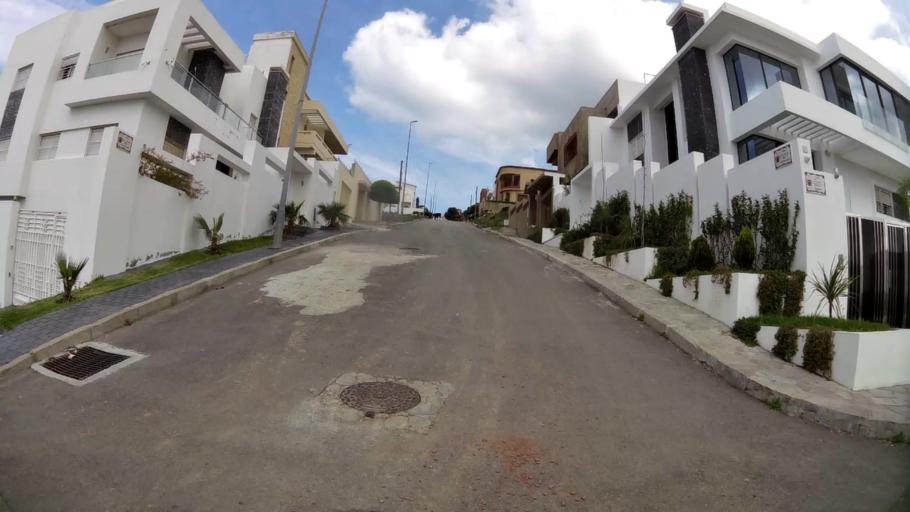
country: MA
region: Tanger-Tetouan
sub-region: Tanger-Assilah
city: Tangier
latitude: 35.7715
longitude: -5.7558
